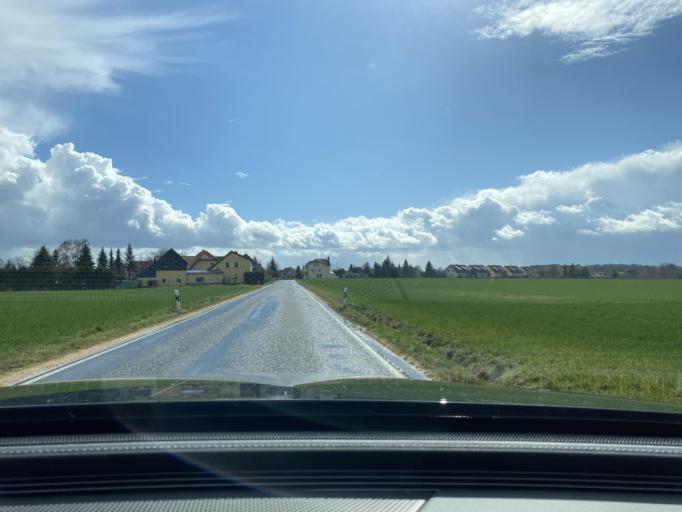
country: DE
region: Saxony
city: Grossdubrau
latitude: 51.2765
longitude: 14.4344
